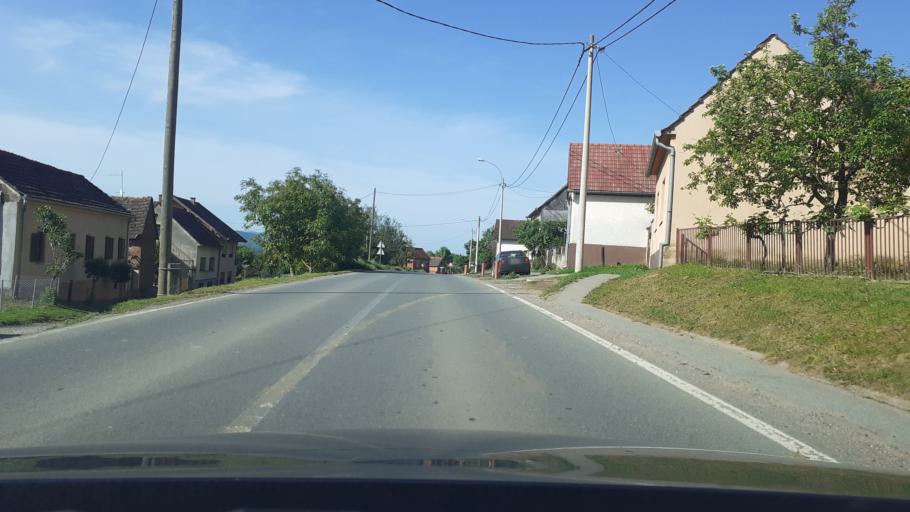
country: HR
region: Pozesko-Slavonska
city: Pleternica
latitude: 45.2654
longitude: 17.7713
